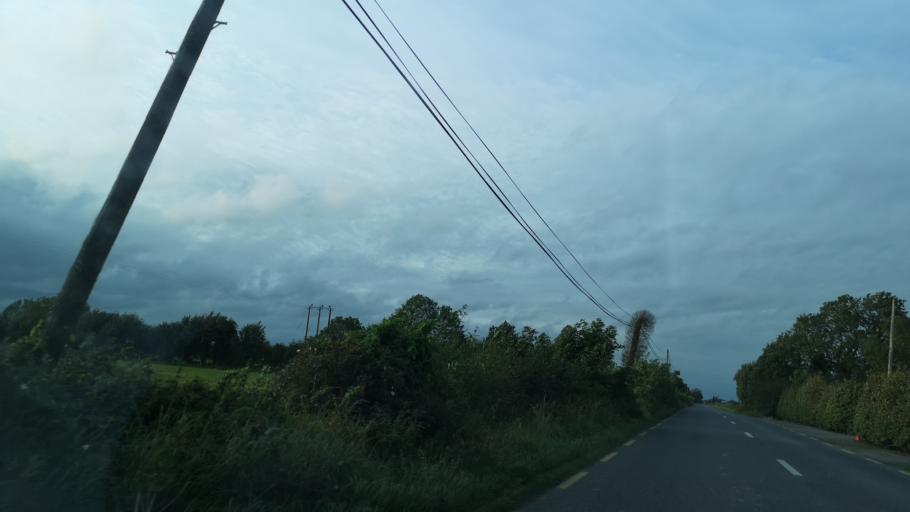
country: IE
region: Leinster
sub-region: Uibh Fhaili
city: Ferbane
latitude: 53.3192
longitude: -7.8214
